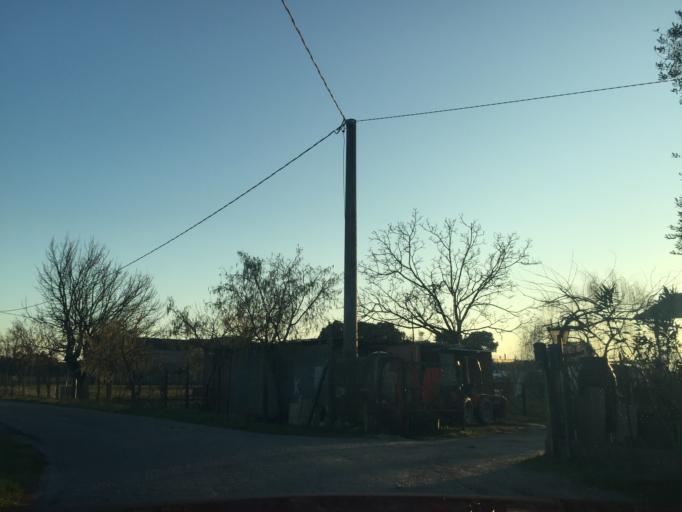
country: IT
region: Tuscany
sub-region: Provincia di Pistoia
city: Anchione
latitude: 43.8379
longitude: 10.7582
